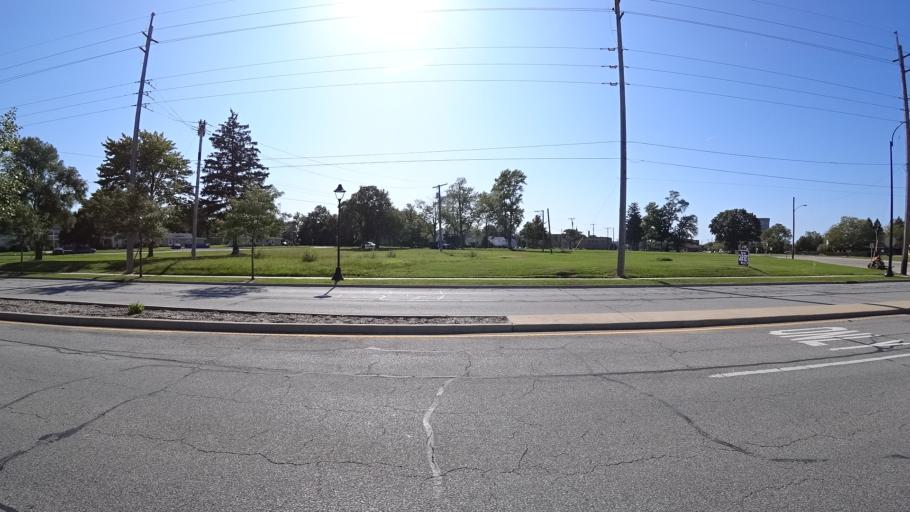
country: US
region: Indiana
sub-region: LaPorte County
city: Michigan City
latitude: 41.7184
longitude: -86.8966
